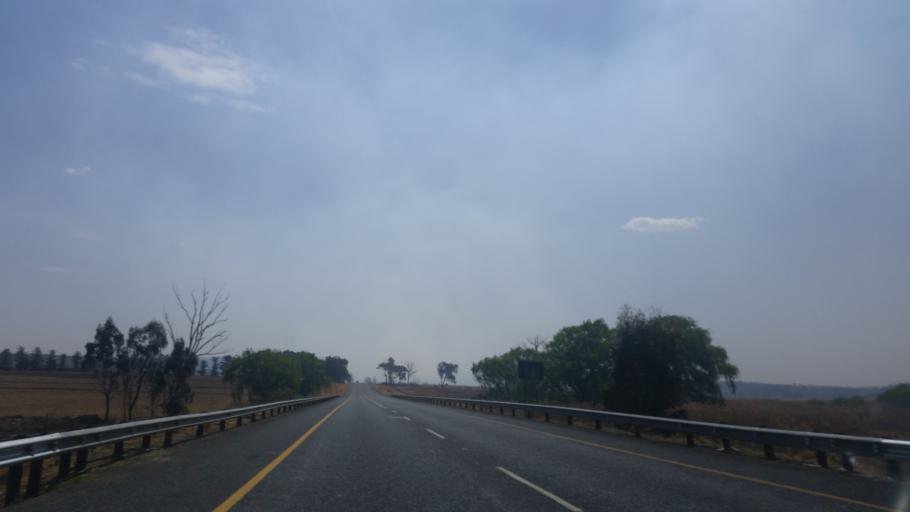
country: ZA
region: Orange Free State
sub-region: Thabo Mofutsanyana District Municipality
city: Bethlehem
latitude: -28.2722
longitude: 28.3725
